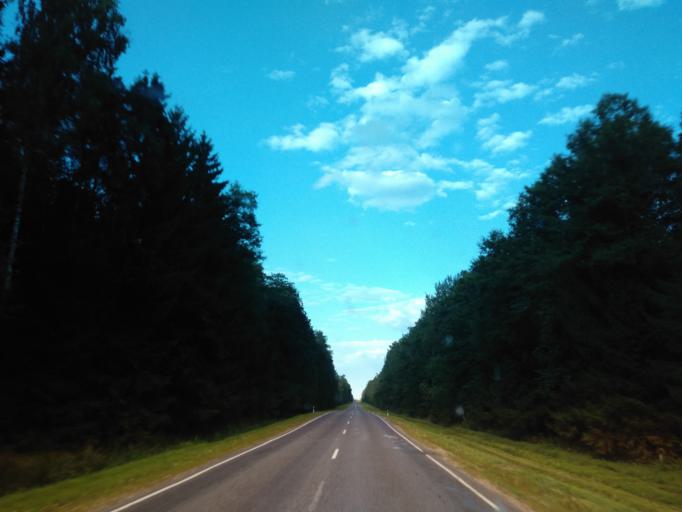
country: BY
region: Minsk
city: Uzda
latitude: 53.4296
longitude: 27.4603
